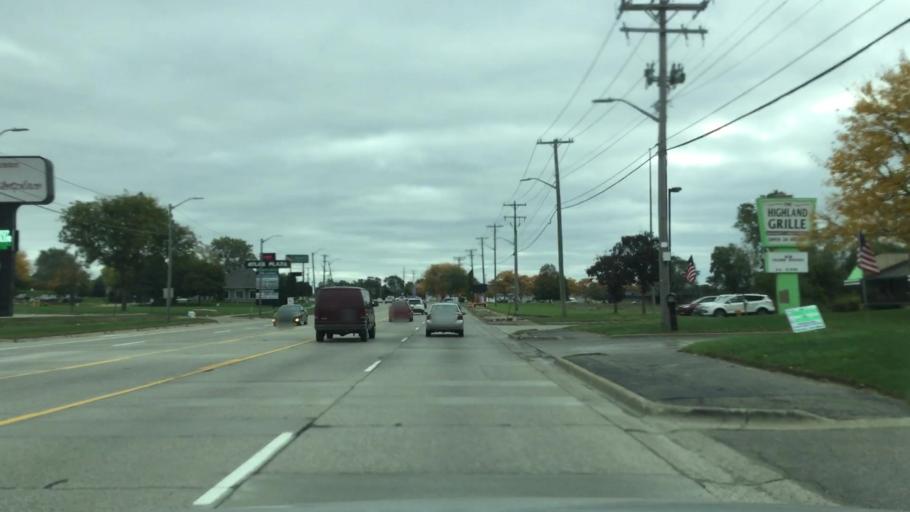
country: US
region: Michigan
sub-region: Oakland County
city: Waterford
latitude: 42.6601
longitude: -83.4298
